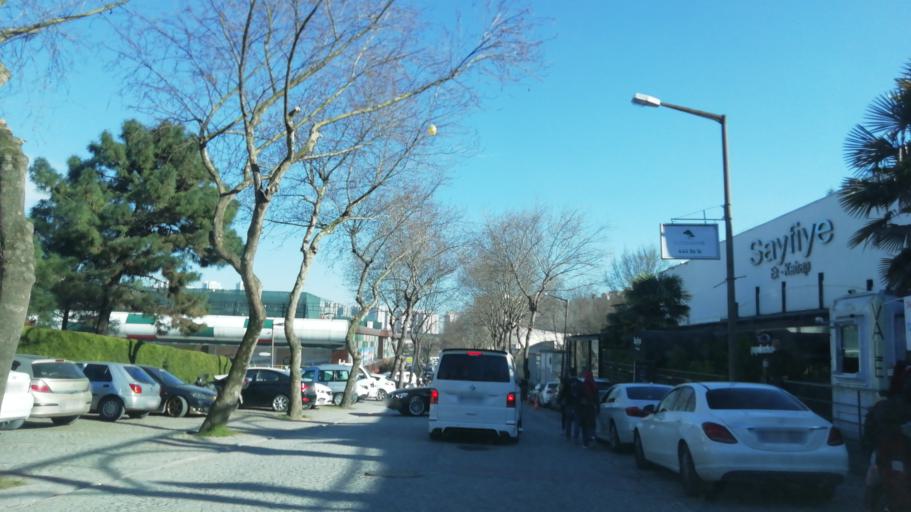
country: TR
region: Istanbul
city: Esenyurt
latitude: 41.0683
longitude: 28.6894
